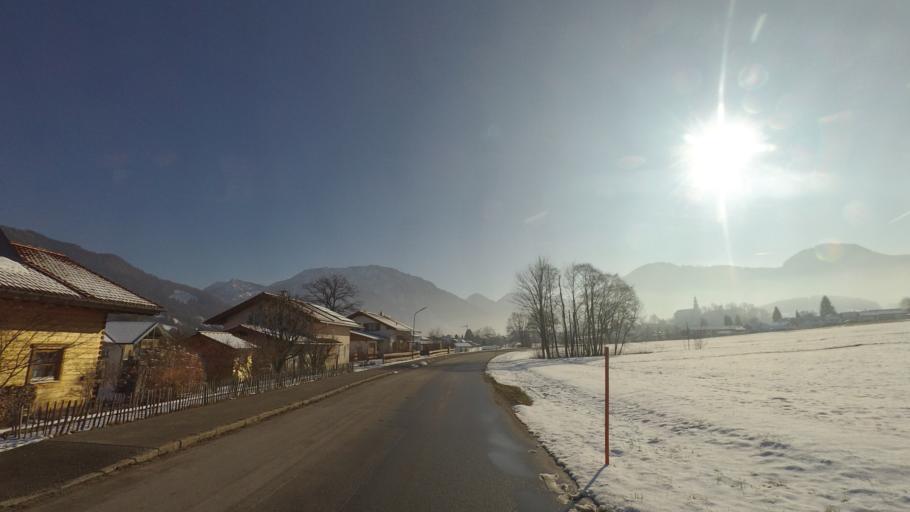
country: DE
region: Bavaria
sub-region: Upper Bavaria
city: Ruhpolding
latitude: 47.7705
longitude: 12.6429
